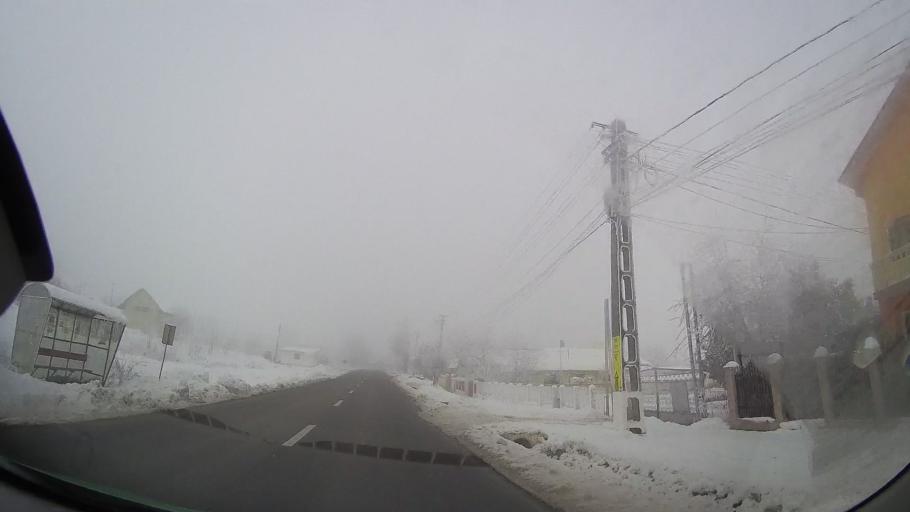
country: RO
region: Iasi
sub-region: Comuna Mircesti
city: Mircesti
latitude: 47.0926
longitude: 26.8209
